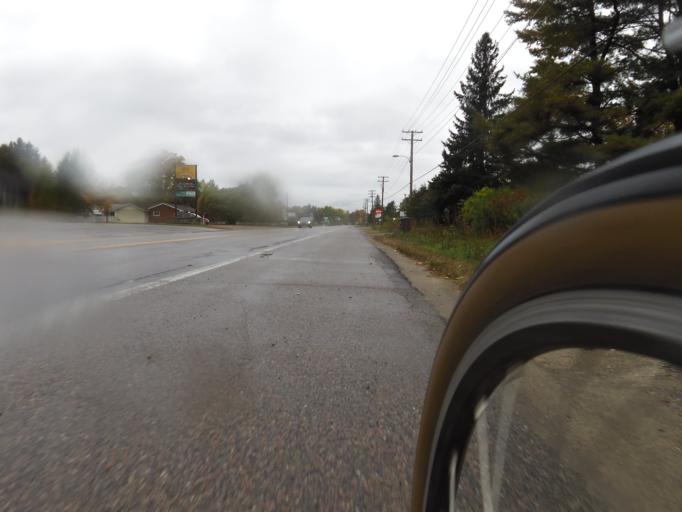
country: CA
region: Quebec
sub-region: Outaouais
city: Fort-Coulonge
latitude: 45.8527
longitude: -76.7334
